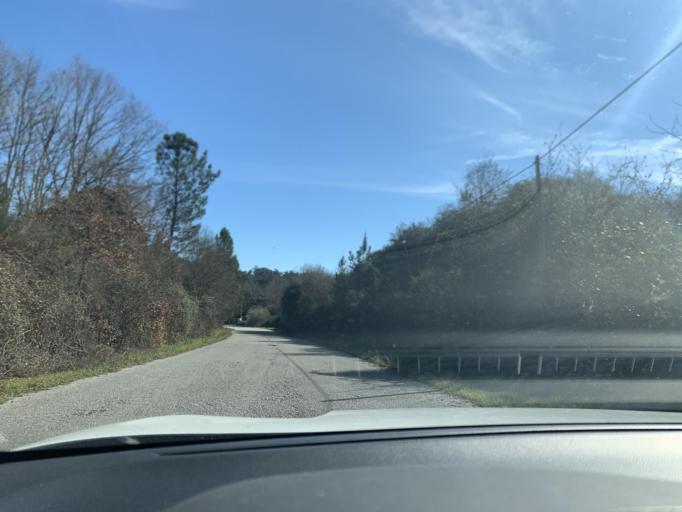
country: PT
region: Viseu
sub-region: Concelho de Tondela
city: Tondela
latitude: 40.5987
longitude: -8.0264
